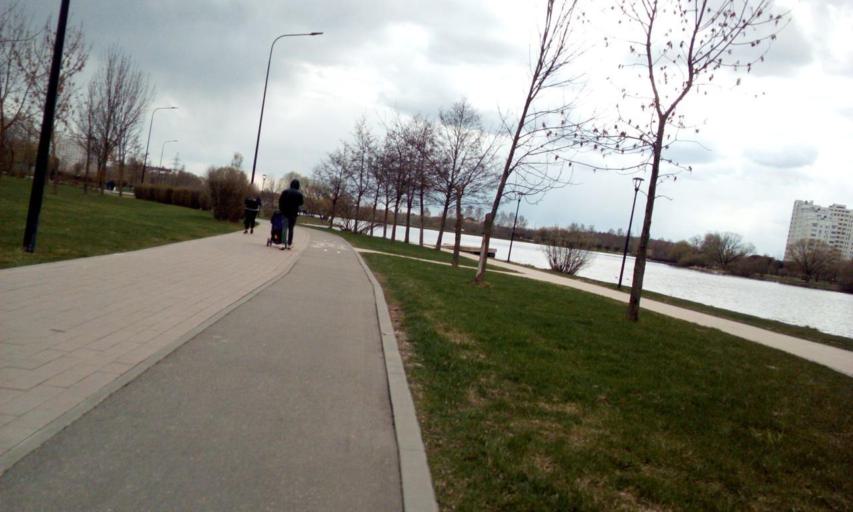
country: RU
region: Moskovskaya
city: Kommunarka
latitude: 55.5339
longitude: 37.5113
